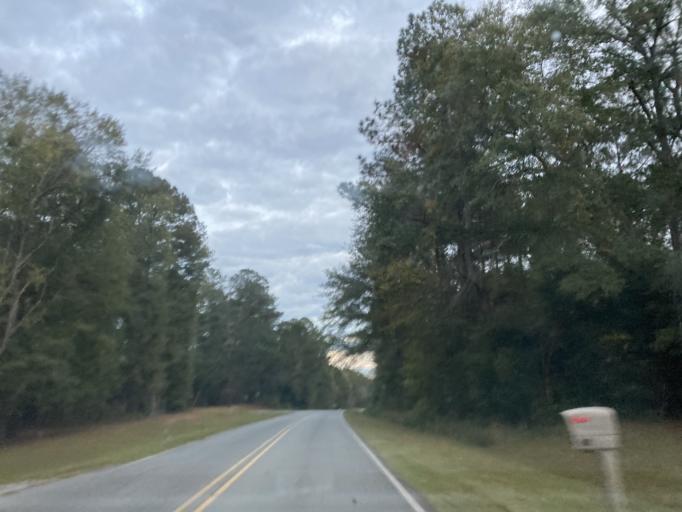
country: US
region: Georgia
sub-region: Jones County
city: Gray
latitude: 32.9739
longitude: -83.5165
